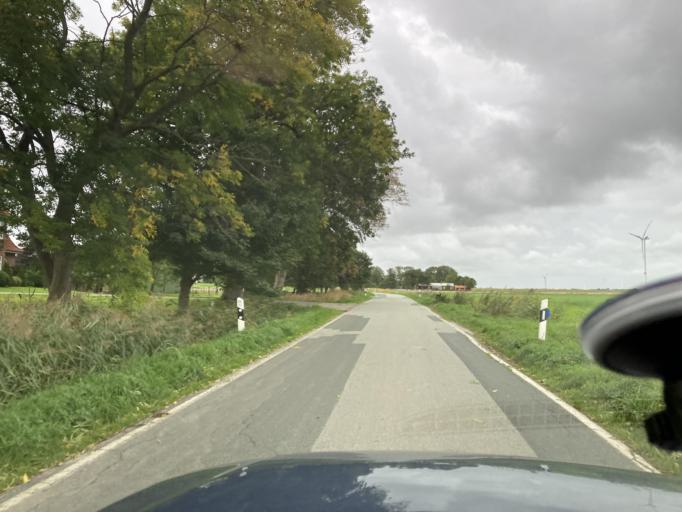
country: DE
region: Schleswig-Holstein
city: Norderwohrden
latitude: 54.1968
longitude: 9.0005
